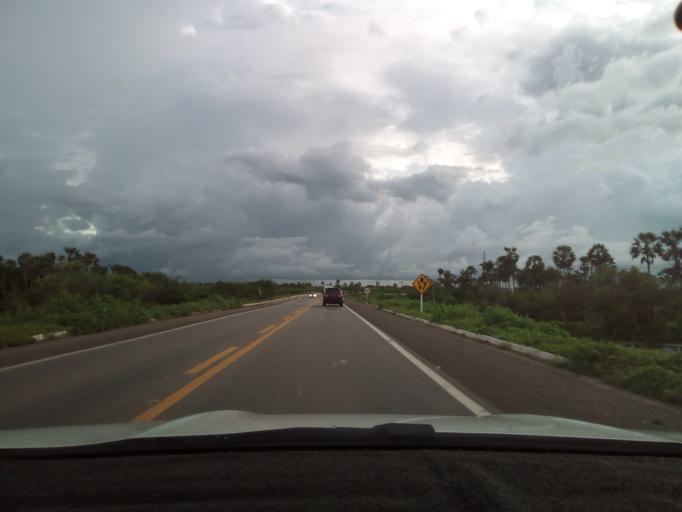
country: BR
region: Ceara
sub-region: Aracati
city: Aracati
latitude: -4.5785
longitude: -37.7701
